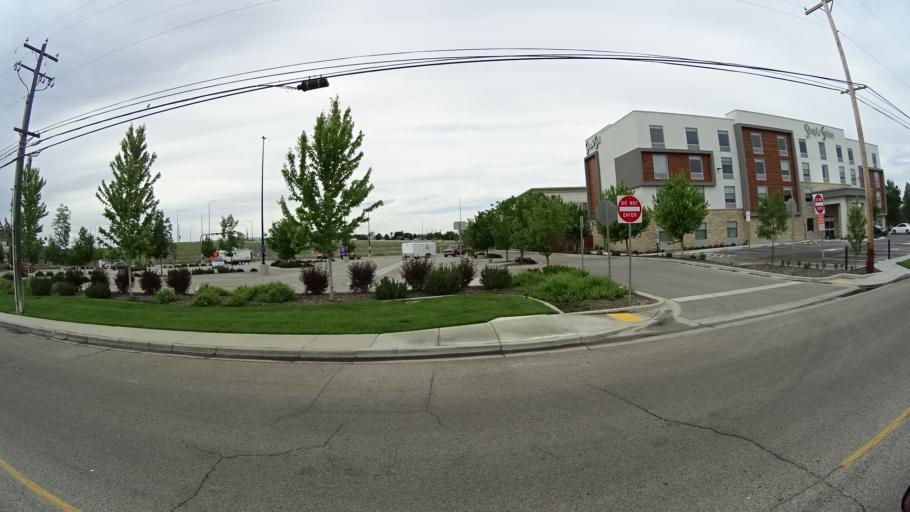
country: US
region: Idaho
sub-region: Ada County
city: Boise
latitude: 43.5735
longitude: -116.2171
